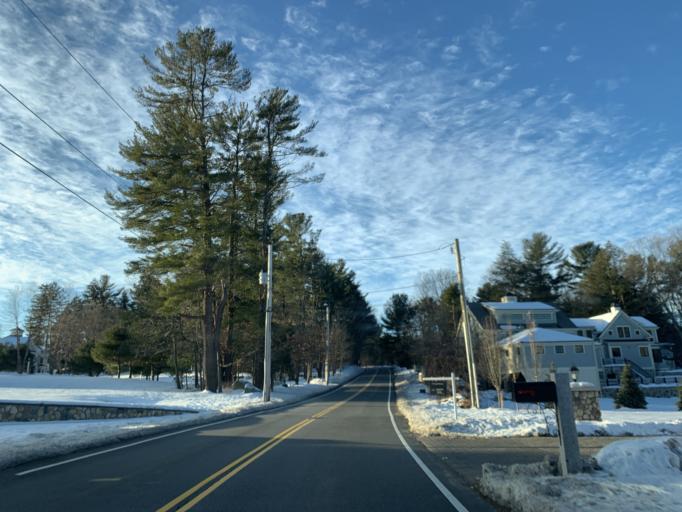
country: US
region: Massachusetts
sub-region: Norfolk County
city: Westwood
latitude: 42.2472
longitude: -71.2216
